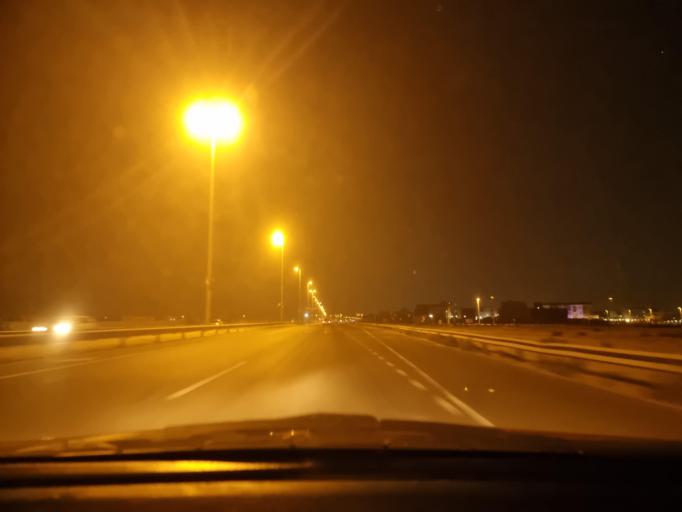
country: AE
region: Abu Dhabi
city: Abu Dhabi
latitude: 24.3704
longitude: 54.6720
